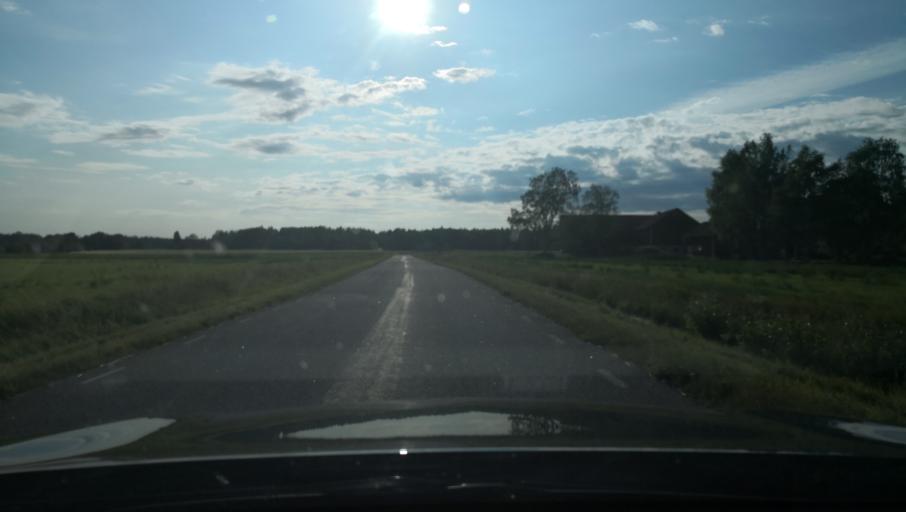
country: SE
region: Uppsala
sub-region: Osthammars Kommun
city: Osterbybruk
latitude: 60.0191
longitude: 17.9726
